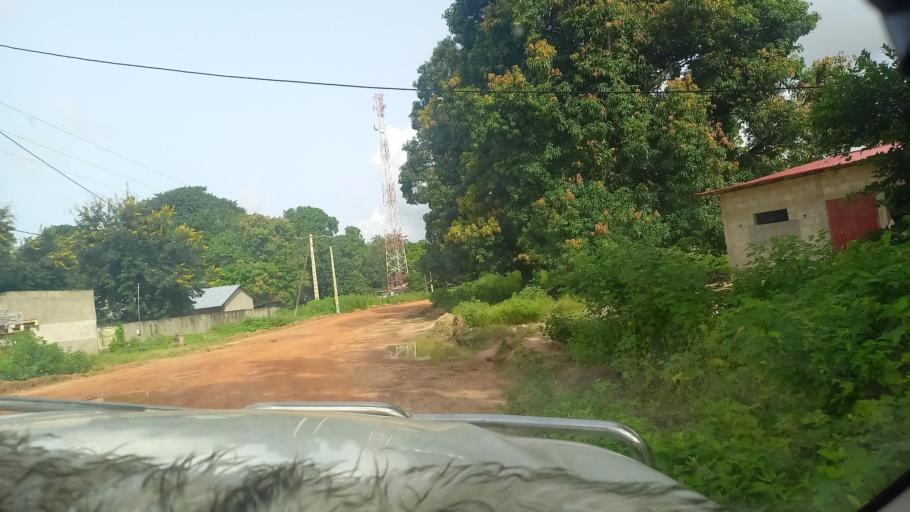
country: SN
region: Ziguinchor
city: Ziguinchor
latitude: 12.6635
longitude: -16.2642
